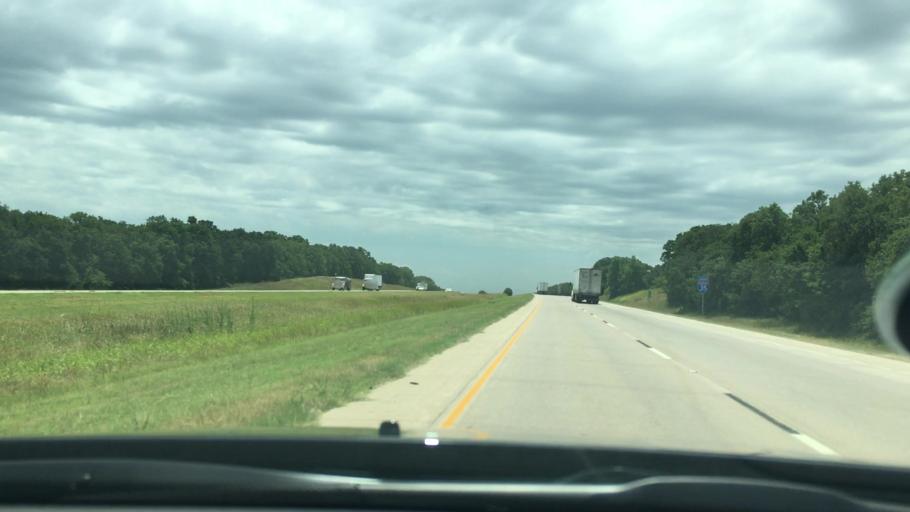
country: US
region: Oklahoma
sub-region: Carter County
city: Ardmore
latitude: 34.0656
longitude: -97.1501
